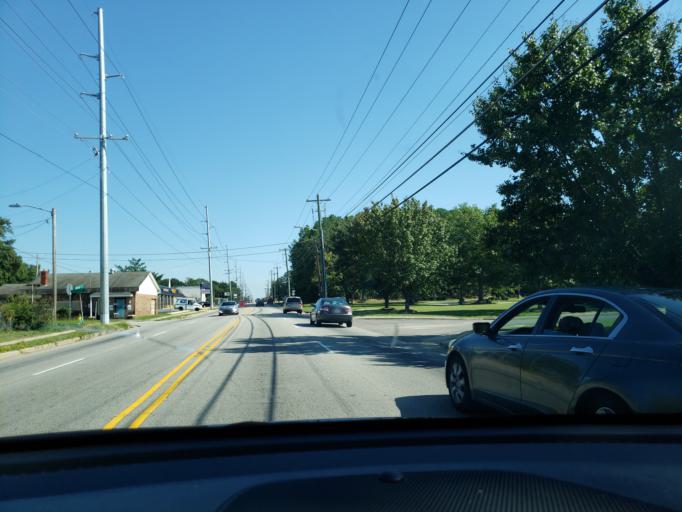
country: US
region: North Carolina
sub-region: Cumberland County
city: Fayetteville
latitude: 35.0890
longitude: -78.9087
